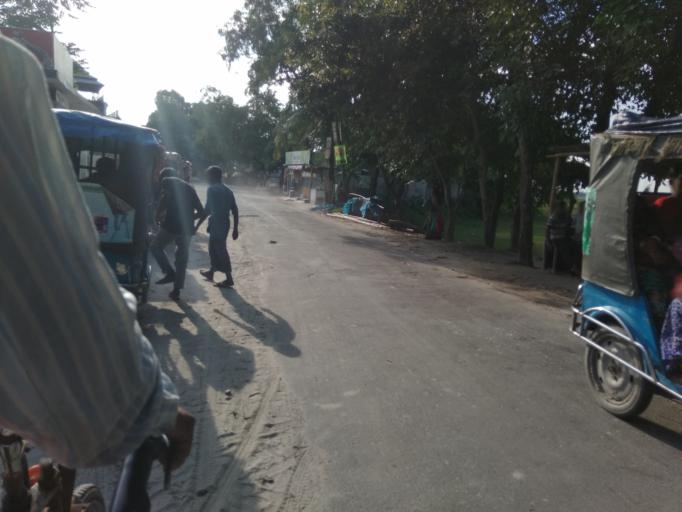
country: BD
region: Rangpur Division
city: Rangpur
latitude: 25.8327
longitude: 89.1123
